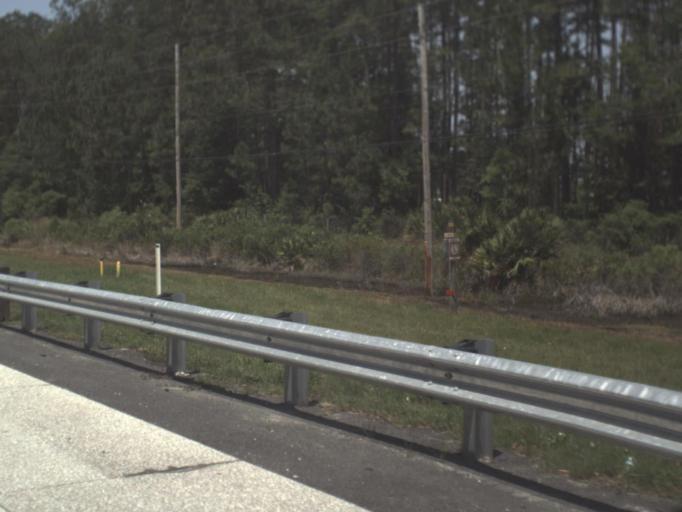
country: US
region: Florida
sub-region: Duval County
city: Baldwin
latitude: 30.2384
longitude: -81.9055
